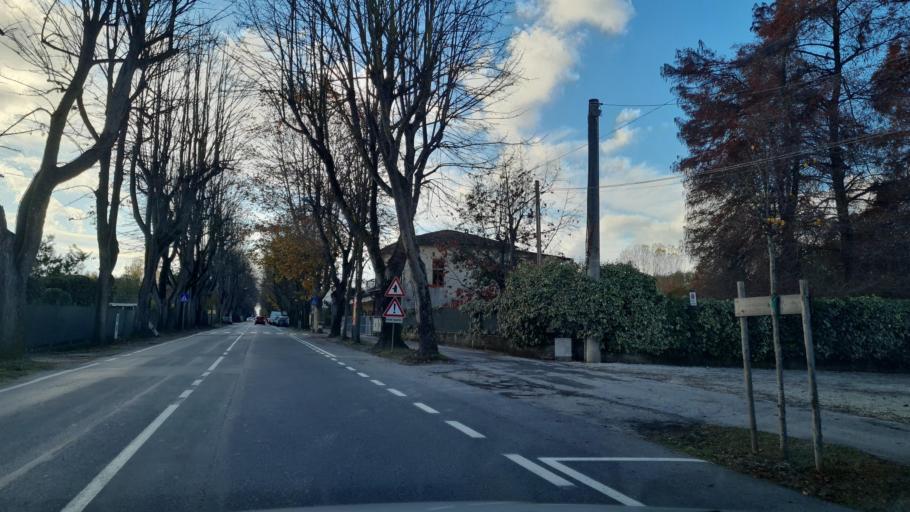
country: IT
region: Tuscany
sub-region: Provincia di Lucca
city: Pietrasanta
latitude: 43.9451
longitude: 10.2054
